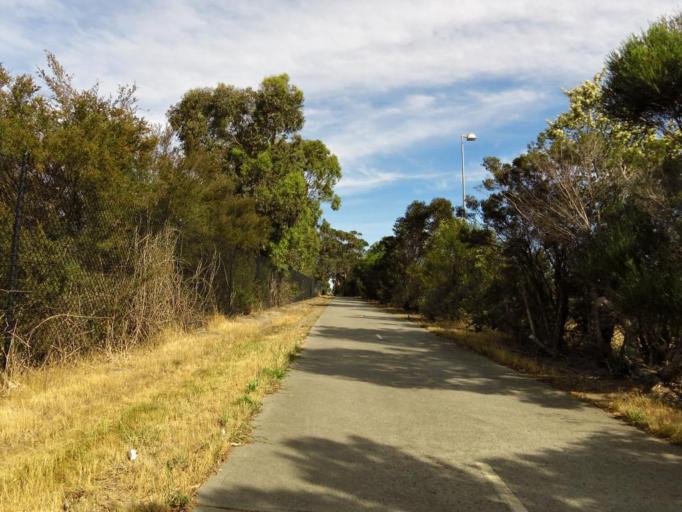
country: AU
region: Victoria
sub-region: Casey
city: Narre Warren
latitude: -38.0168
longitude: 145.3067
